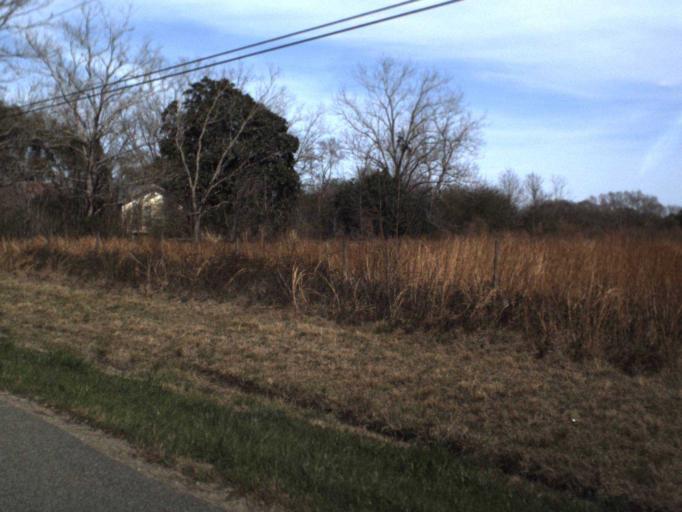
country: US
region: Florida
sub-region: Jackson County
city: Graceville
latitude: 30.8962
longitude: -85.5233
